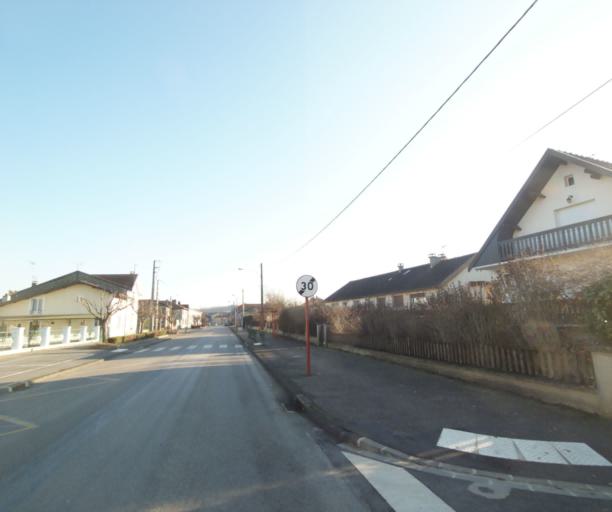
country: FR
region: Champagne-Ardenne
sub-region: Departement de la Haute-Marne
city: Bienville
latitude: 48.5635
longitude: 5.0491
